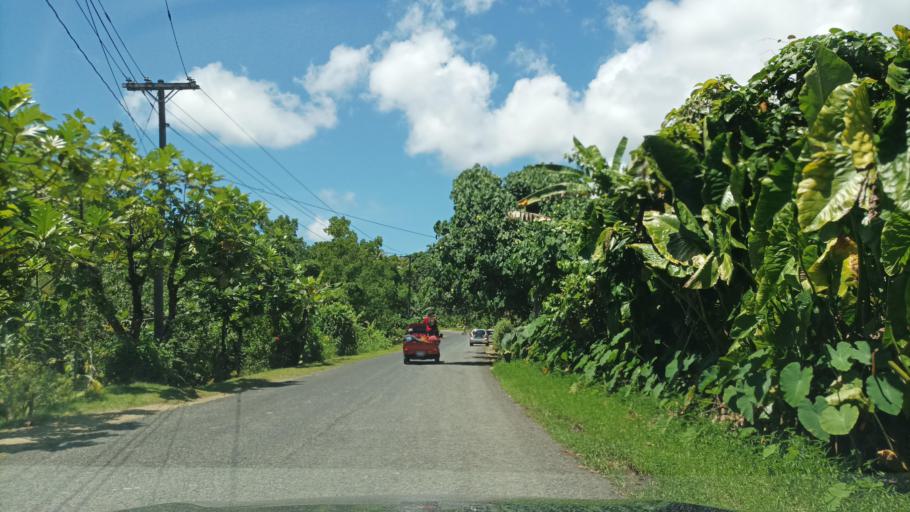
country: FM
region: Pohnpei
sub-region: Kolonia Municipality
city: Kolonia
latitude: 6.9300
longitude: 158.2784
